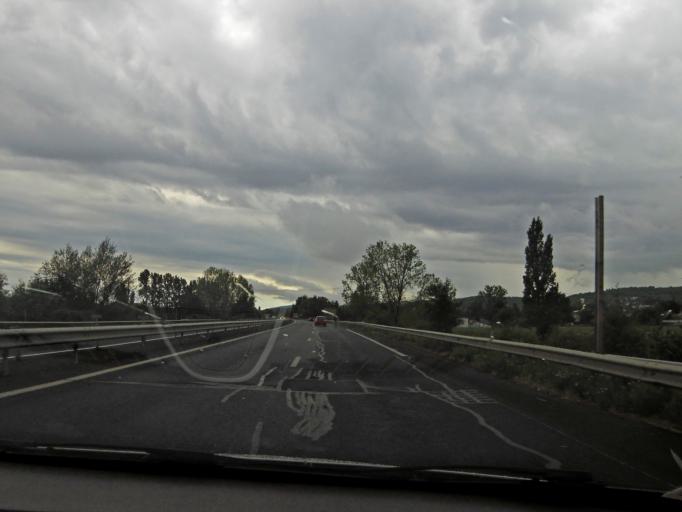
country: FR
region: Auvergne
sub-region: Departement de la Haute-Loire
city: Lempdes-sur-Allagnon
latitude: 45.3929
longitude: 3.2733
